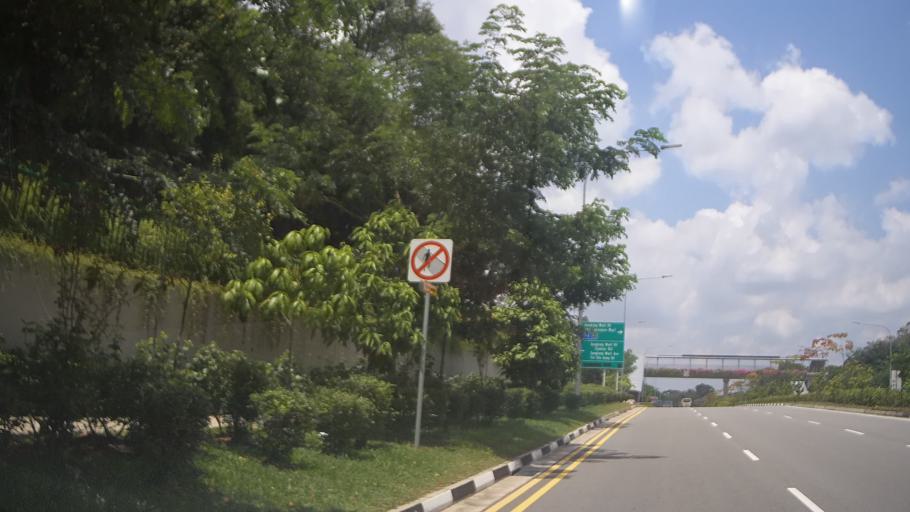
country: MY
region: Johor
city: Kampung Pasir Gudang Baru
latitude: 1.3946
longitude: 103.8720
